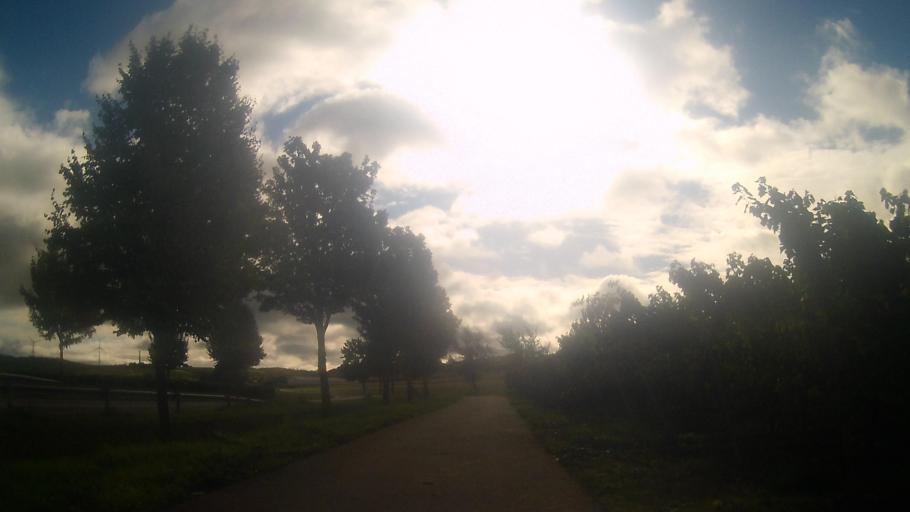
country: DE
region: Rheinland-Pfalz
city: Sulzheim
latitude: 49.8256
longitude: 8.0762
